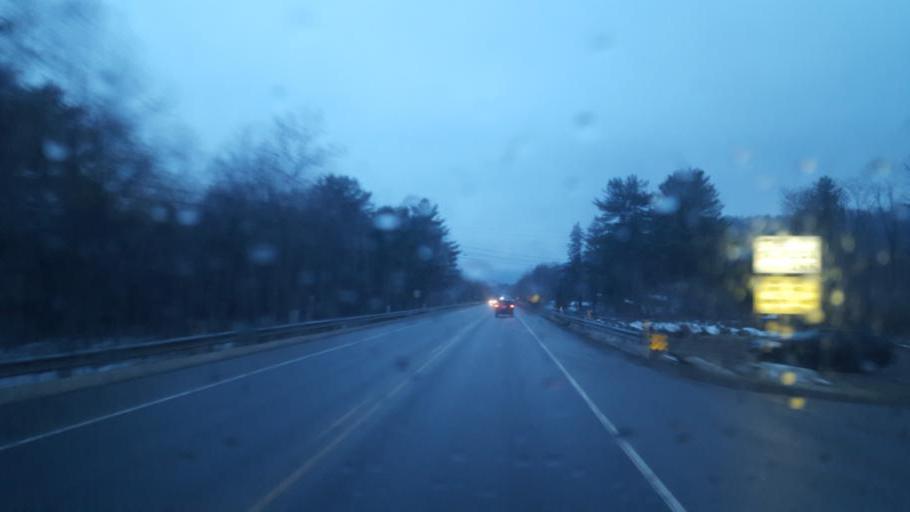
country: US
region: Pennsylvania
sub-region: McKean County
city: Port Allegany
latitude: 41.7960
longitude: -78.2530
